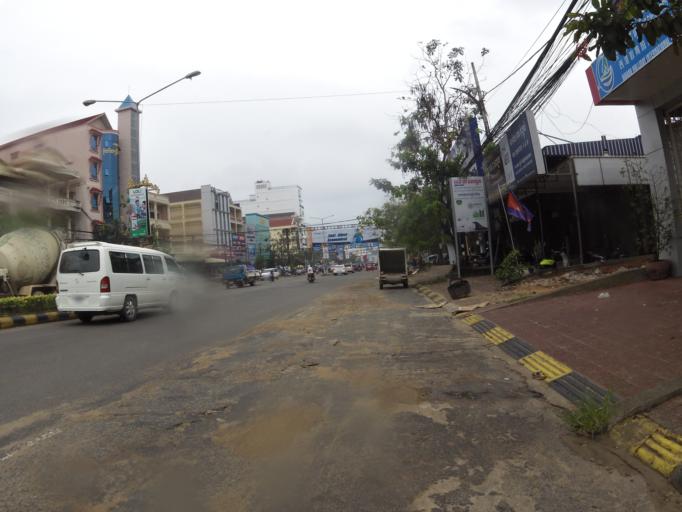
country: KH
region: Preah Sihanouk
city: Sihanoukville
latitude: 10.6241
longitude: 103.5228
